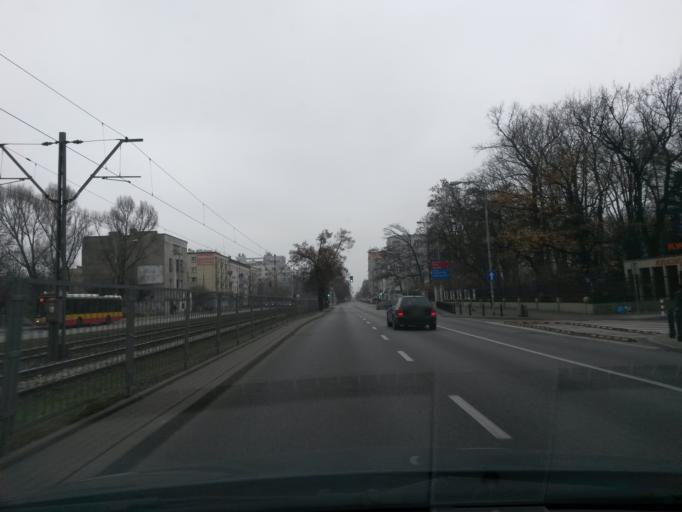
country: PL
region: Masovian Voivodeship
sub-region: Warszawa
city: Mokotow
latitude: 52.1985
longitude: 21.0238
